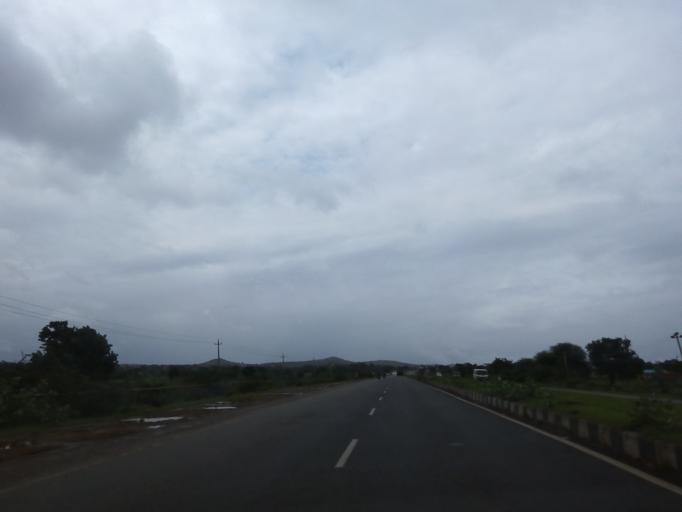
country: IN
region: Karnataka
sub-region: Haveri
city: Byadgi
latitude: 14.7243
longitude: 75.4751
